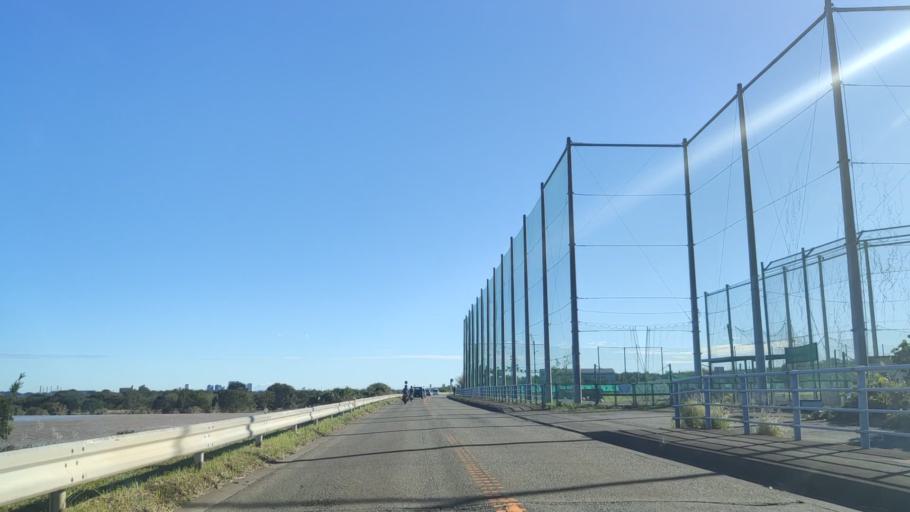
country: JP
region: Kanagawa
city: Zama
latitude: 35.5107
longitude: 139.3742
